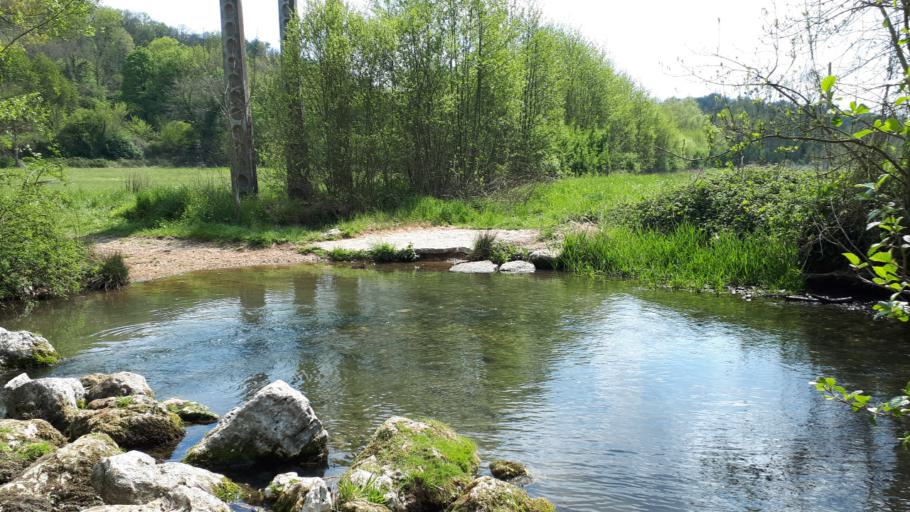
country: FR
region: Centre
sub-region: Departement du Loir-et-Cher
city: Villiers-sur-Loir
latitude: 47.8239
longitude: 0.9745
